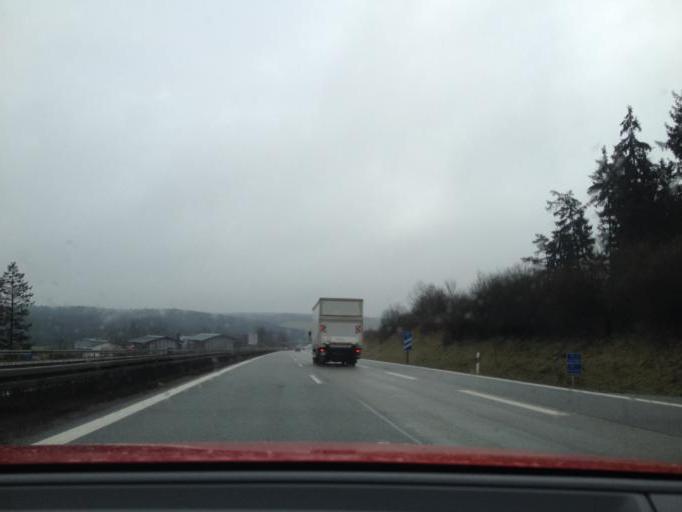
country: DE
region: Bavaria
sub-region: Upper Franconia
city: Rehau
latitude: 50.2646
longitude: 12.0395
